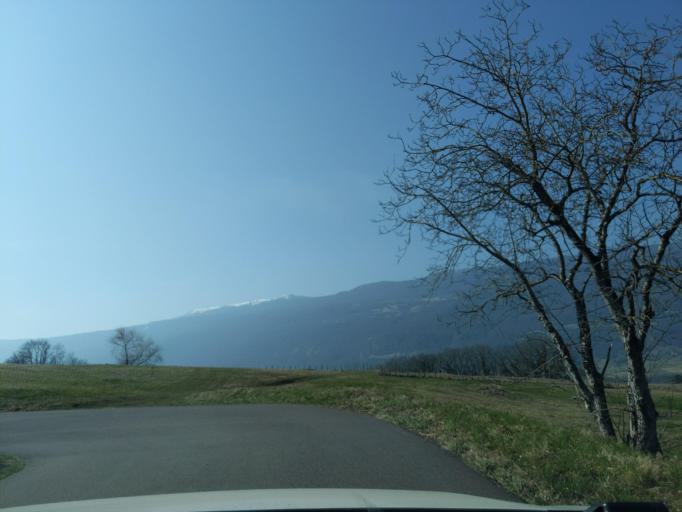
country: FR
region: Rhone-Alpes
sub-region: Departement de la Haute-Savoie
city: Versonnex
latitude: 45.9294
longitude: 5.8403
